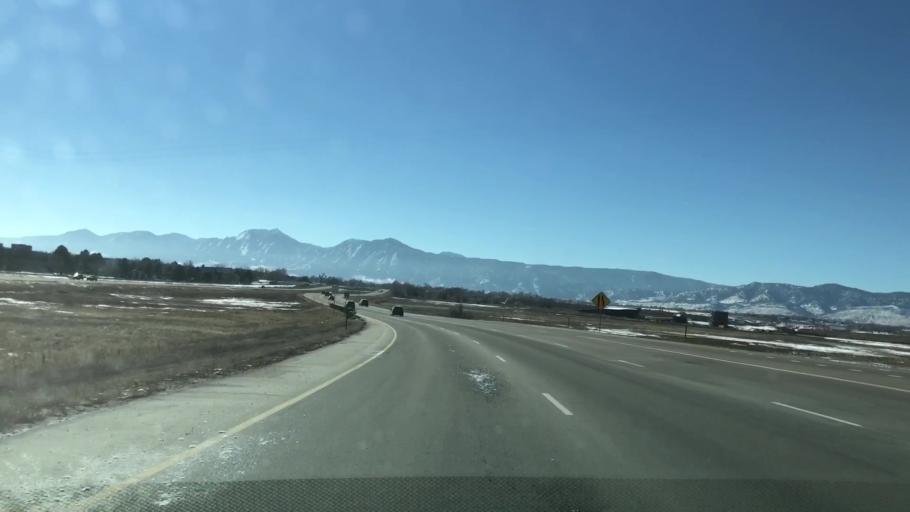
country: US
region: Colorado
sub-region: Boulder County
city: Gunbarrel
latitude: 40.0747
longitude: -105.2071
